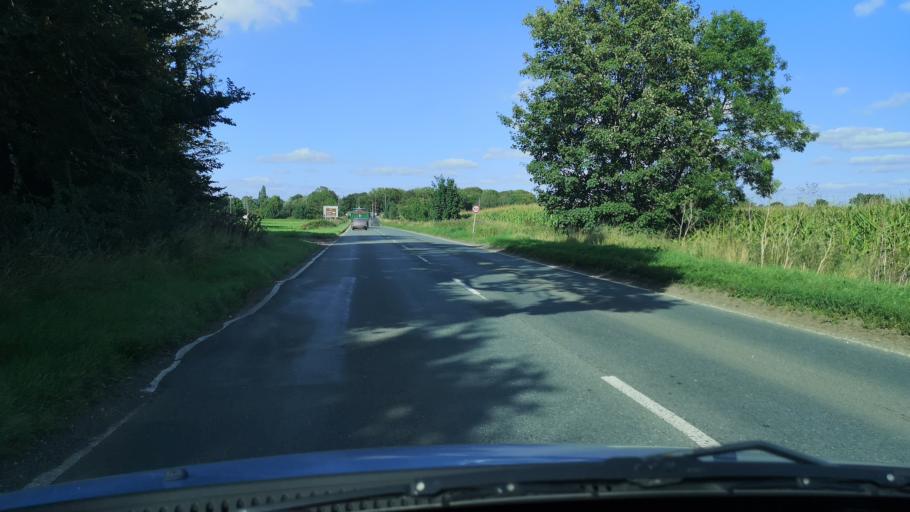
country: GB
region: England
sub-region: North Lincolnshire
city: Crowle
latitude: 53.5828
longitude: -0.8202
